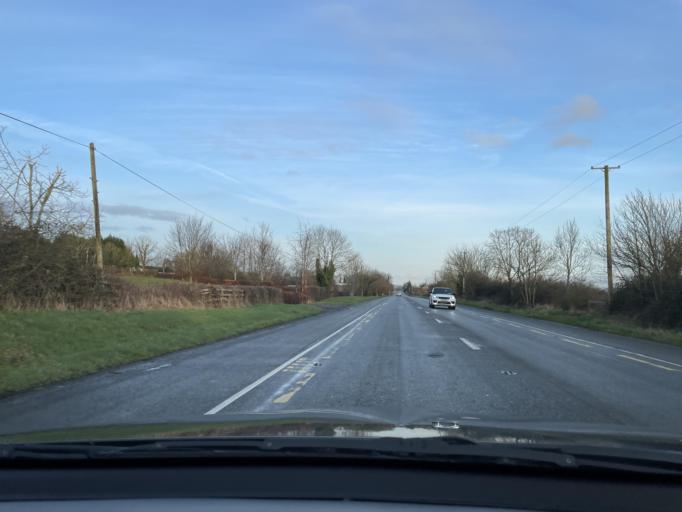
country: IE
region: Leinster
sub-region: Kilkenny
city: Thomastown
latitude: 52.6473
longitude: -7.1206
